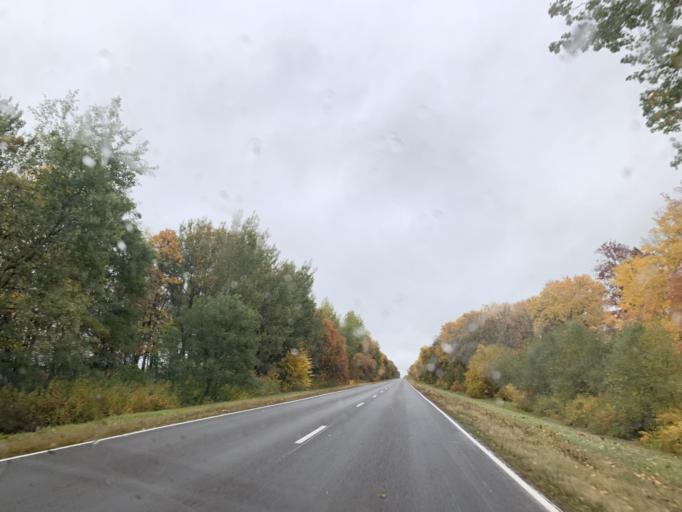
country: BY
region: Minsk
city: Haradzyeya
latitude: 53.4095
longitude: 26.6098
